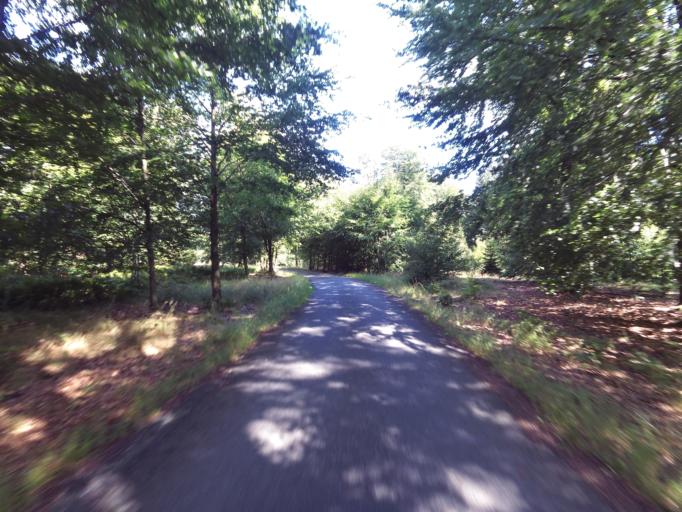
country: BE
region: Wallonia
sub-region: Province du Luxembourg
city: Nassogne
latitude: 50.1069
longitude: 5.3825
